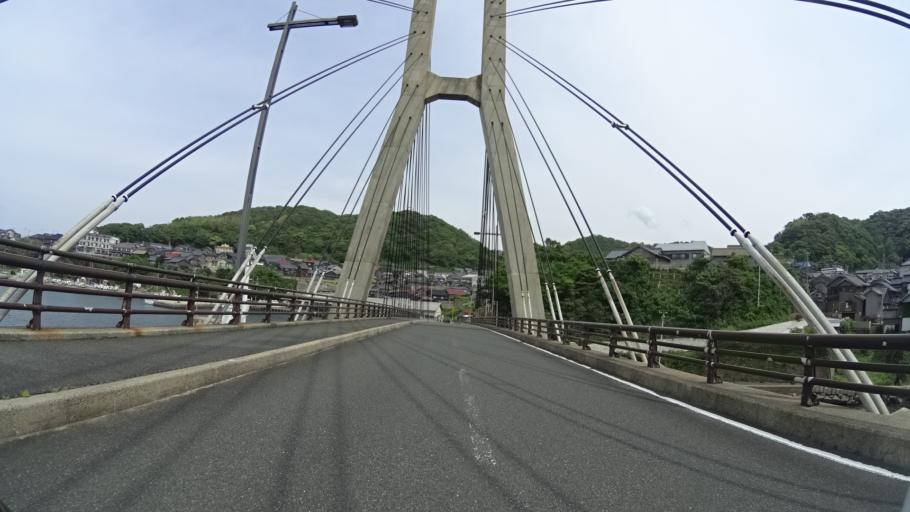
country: JP
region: Kyoto
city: Miyazu
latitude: 35.7389
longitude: 135.0912
